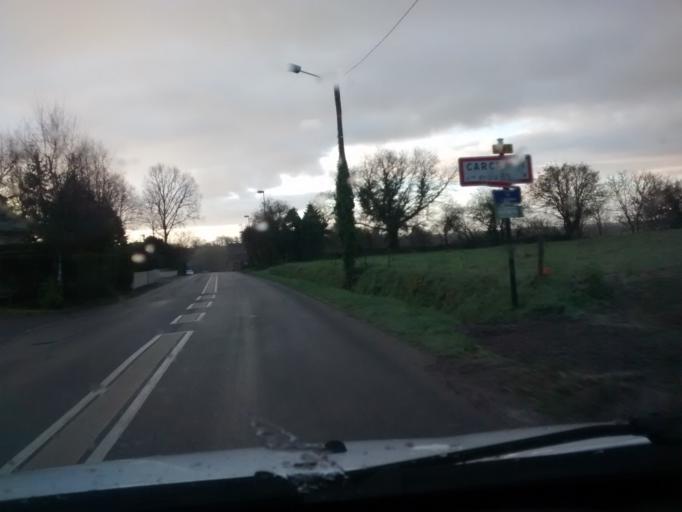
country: FR
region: Brittany
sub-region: Departement d'Ille-et-Vilaine
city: Domalain
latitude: 47.9678
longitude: -1.2666
